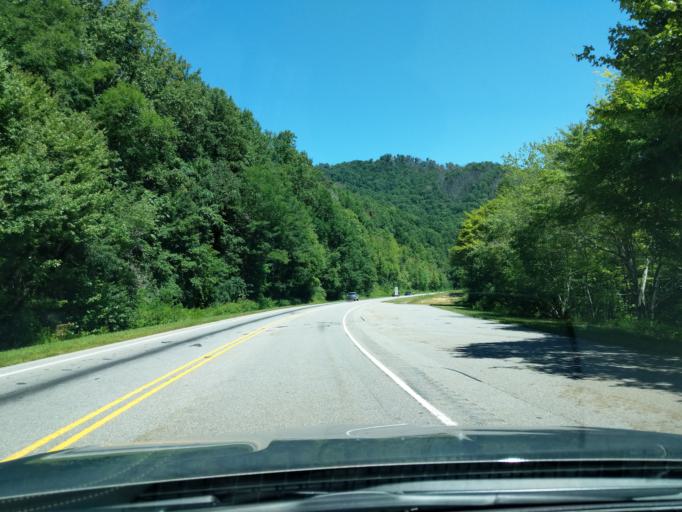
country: US
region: North Carolina
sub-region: Macon County
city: Franklin
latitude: 35.1286
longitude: -83.5389
